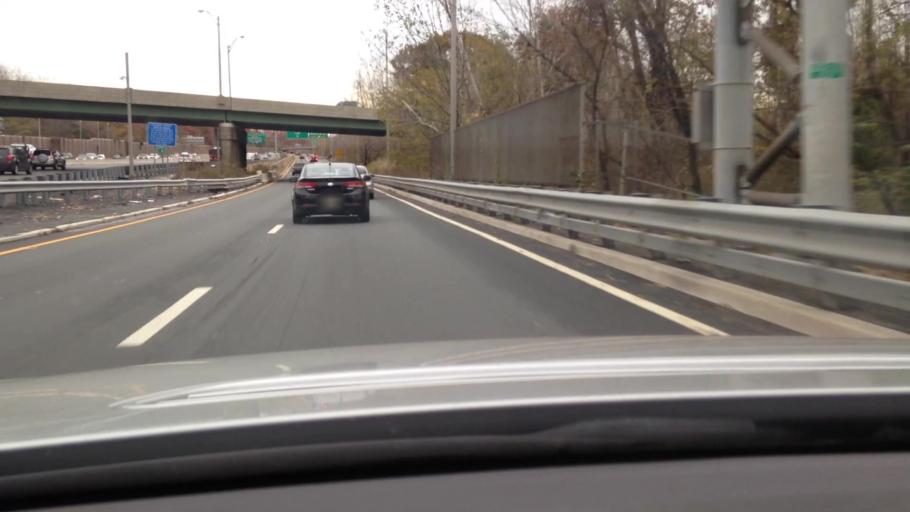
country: US
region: New Jersey
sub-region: Bergen County
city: Saddle Brook
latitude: 40.9032
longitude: -74.0990
